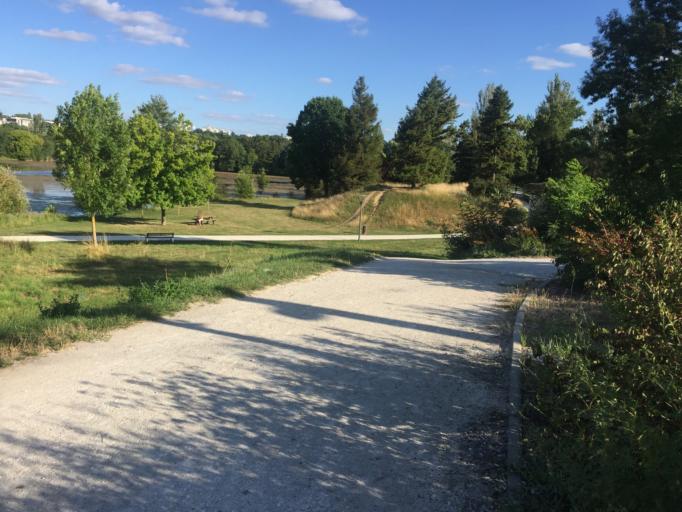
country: FR
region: Centre
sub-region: Departement d'Indre-et-Loire
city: Tours
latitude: 47.3679
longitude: 0.6871
